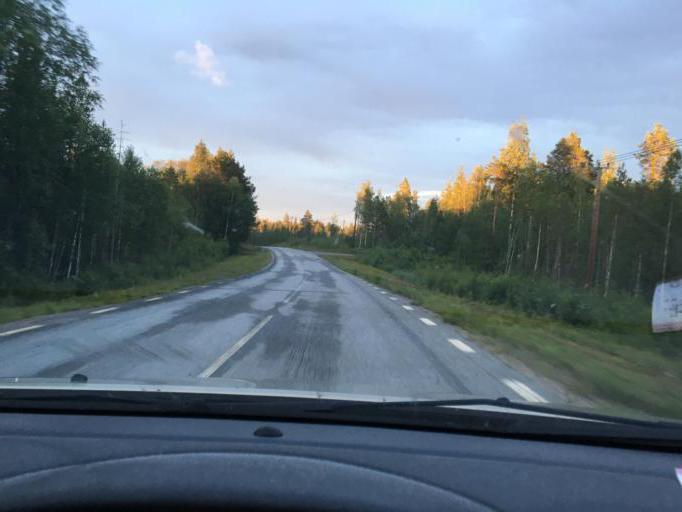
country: SE
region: Norrbotten
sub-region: Kalix Kommun
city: Toere
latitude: 66.0642
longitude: 22.6666
